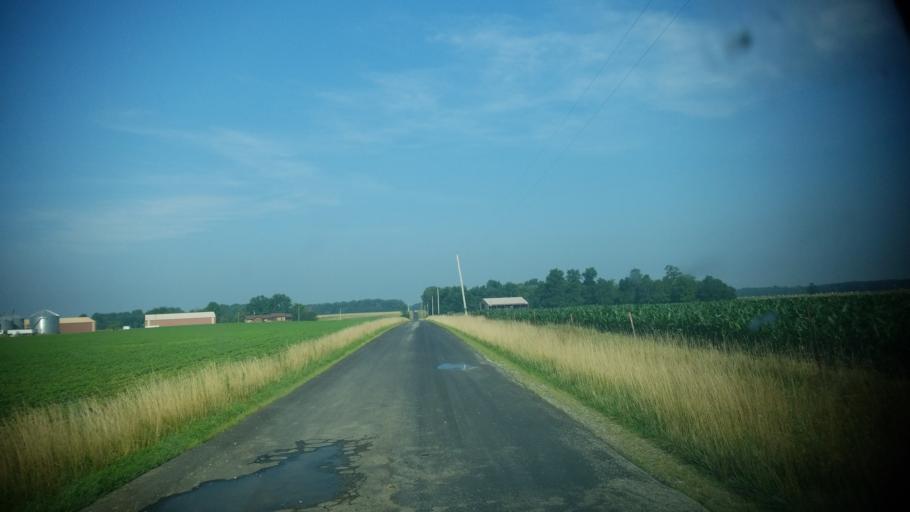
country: US
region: Illinois
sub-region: Clay County
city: Flora
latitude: 38.6024
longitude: -88.3838
